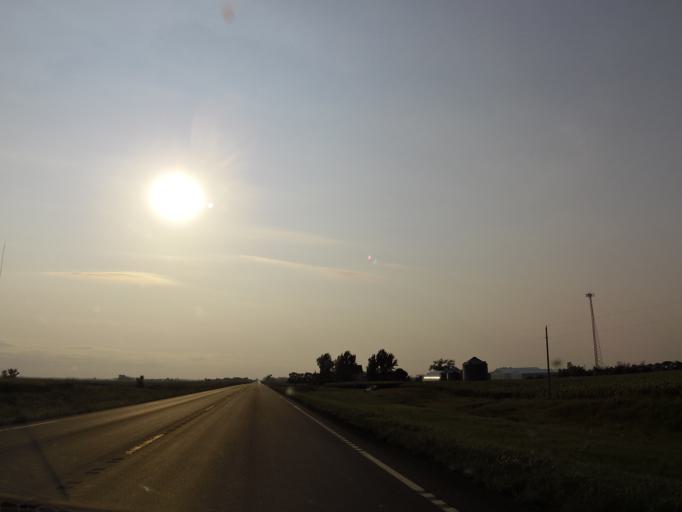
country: US
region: North Dakota
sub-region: Traill County
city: Mayville
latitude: 47.3529
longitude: -97.2593
